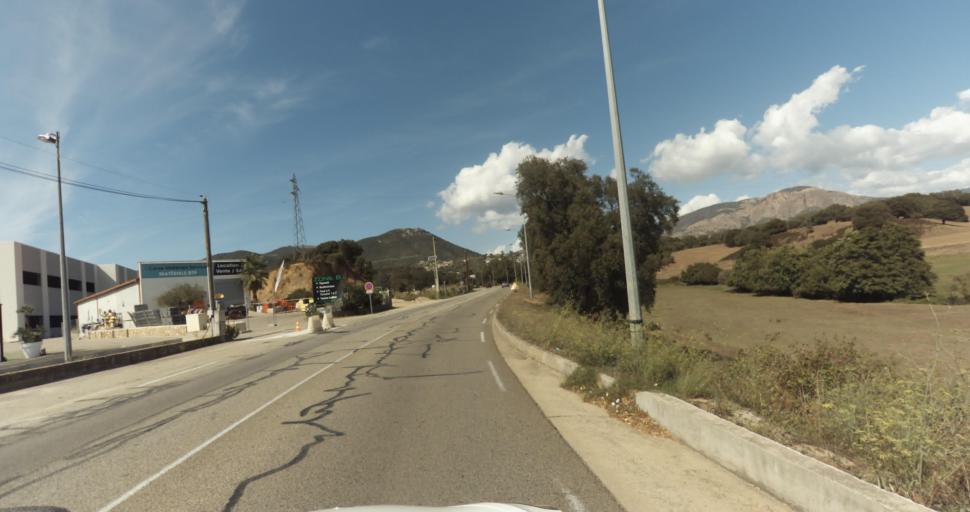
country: FR
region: Corsica
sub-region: Departement de la Corse-du-Sud
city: Afa
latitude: 41.9561
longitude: 8.7823
